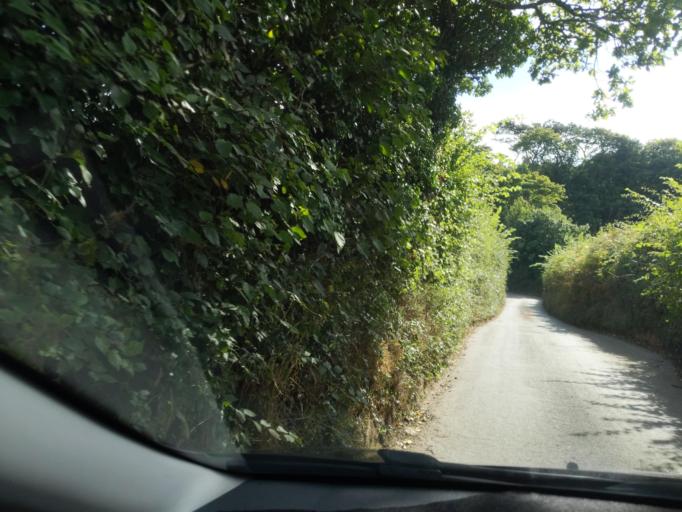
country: GB
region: England
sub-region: Cornwall
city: Torpoint
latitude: 50.3584
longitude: -4.2351
